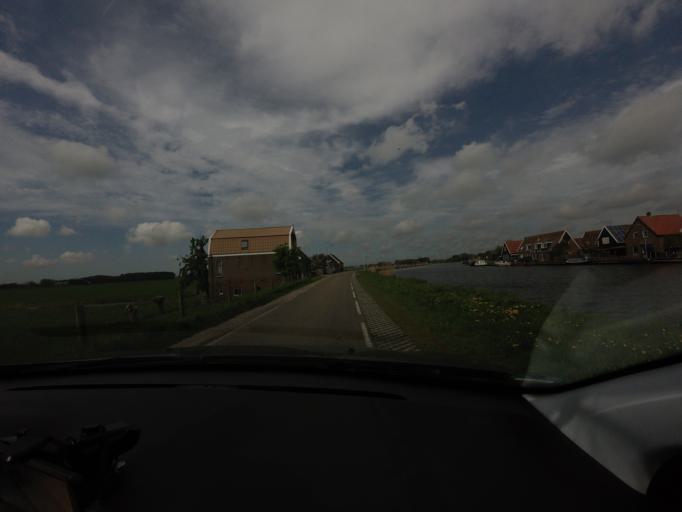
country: NL
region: North Holland
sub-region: Gemeente Zaanstad
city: Zaanstad
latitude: 52.5449
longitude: 4.8117
